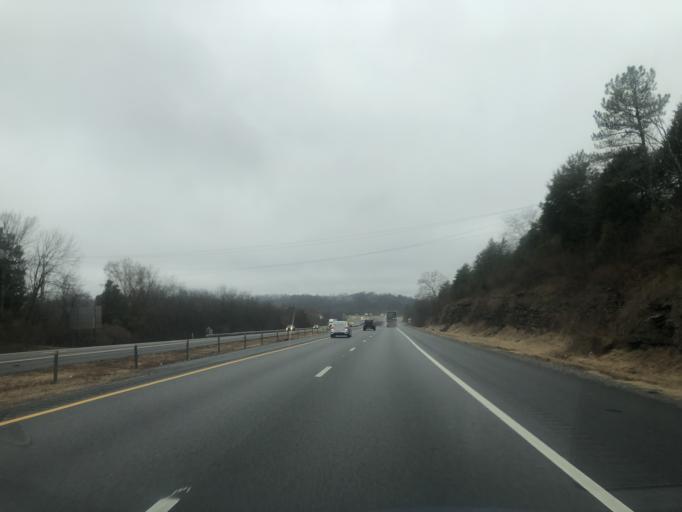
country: US
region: Tennessee
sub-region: Cheatham County
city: Pegram
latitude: 36.0747
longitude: -86.9777
